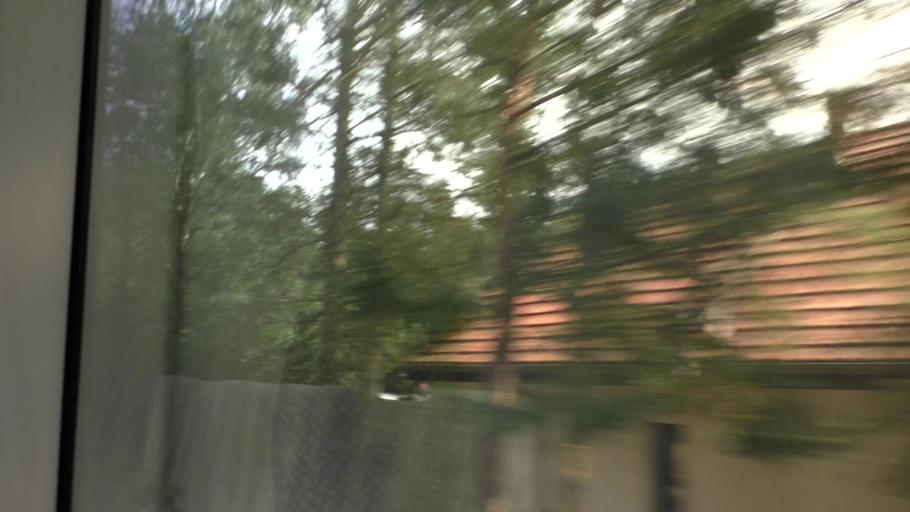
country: DE
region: Brandenburg
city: Konigs Wusterhausen
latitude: 52.2990
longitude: 13.6737
